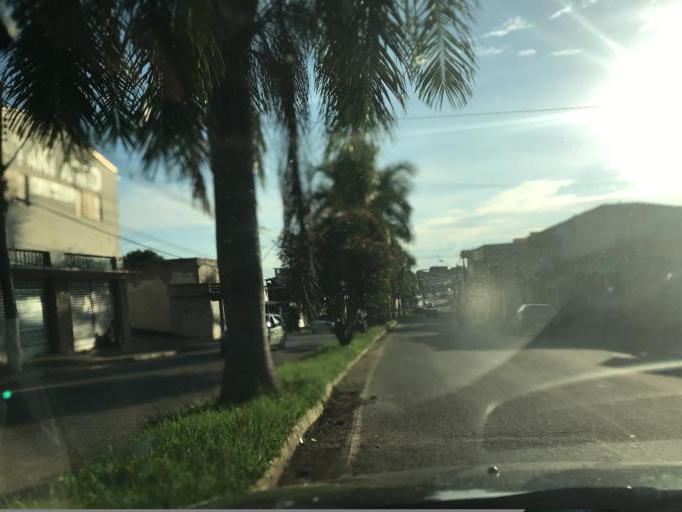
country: BR
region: Minas Gerais
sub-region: Tres Coracoes
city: Tres Coracoes
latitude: -21.6921
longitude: -45.2411
